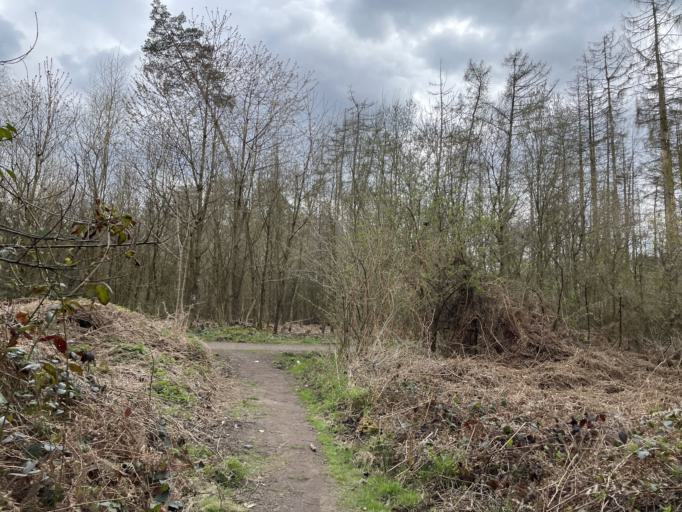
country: DE
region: North Rhine-Westphalia
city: Porta Westfalica
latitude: 52.2269
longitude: 8.9253
